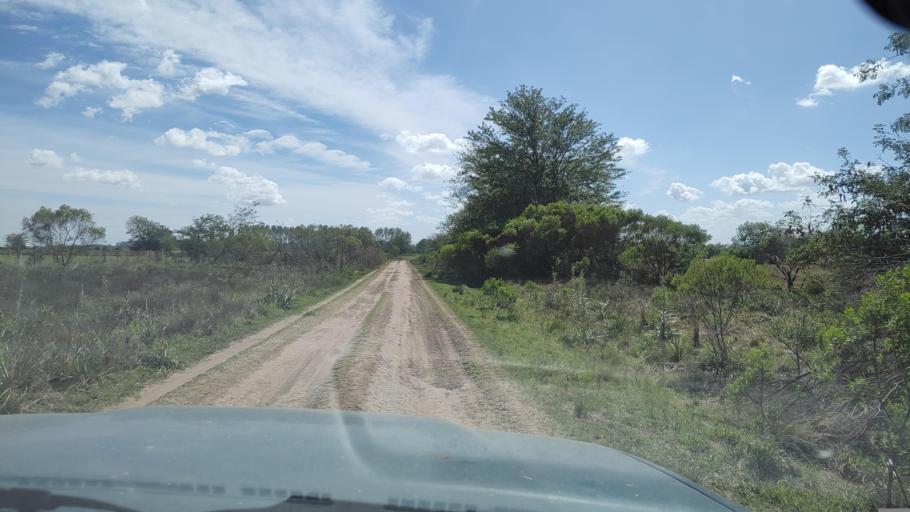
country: AR
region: Buenos Aires
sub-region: Partido de Lujan
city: Lujan
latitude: -34.5182
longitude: -59.1630
